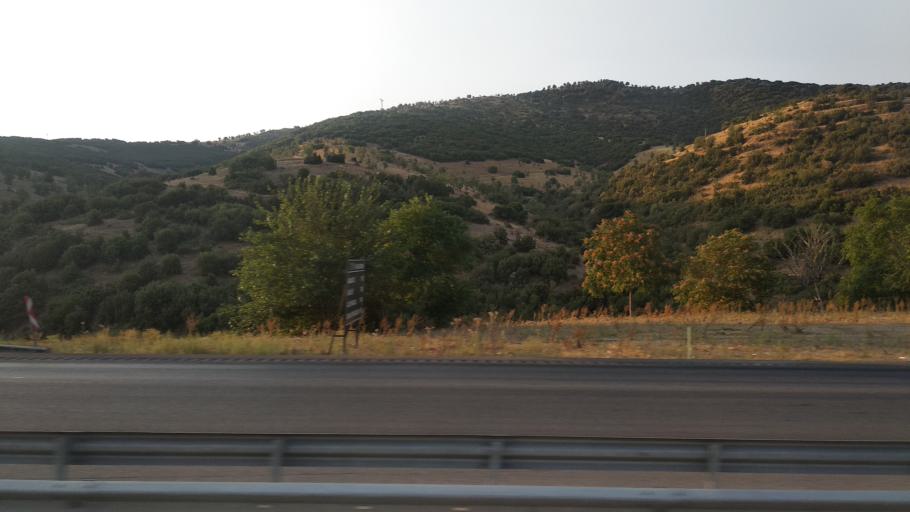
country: TR
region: Manisa
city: Menye
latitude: 38.5515
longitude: 28.4620
